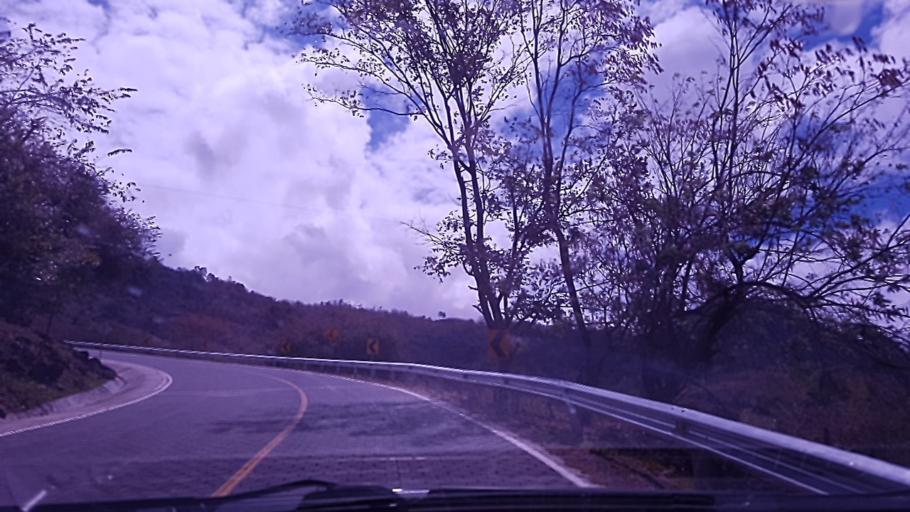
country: NI
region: Esteli
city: Condega
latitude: 13.4083
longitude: -86.2918
